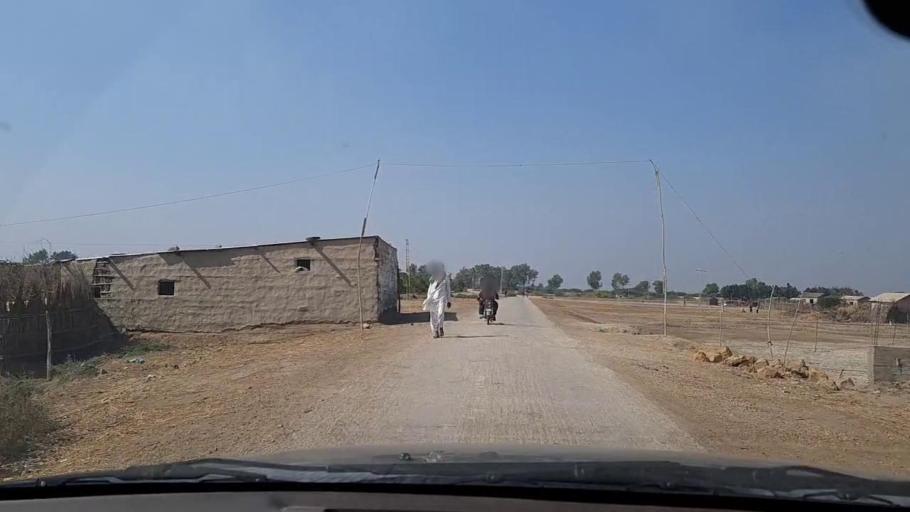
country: PK
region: Sindh
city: Chuhar Jamali
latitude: 24.4222
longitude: 67.8216
